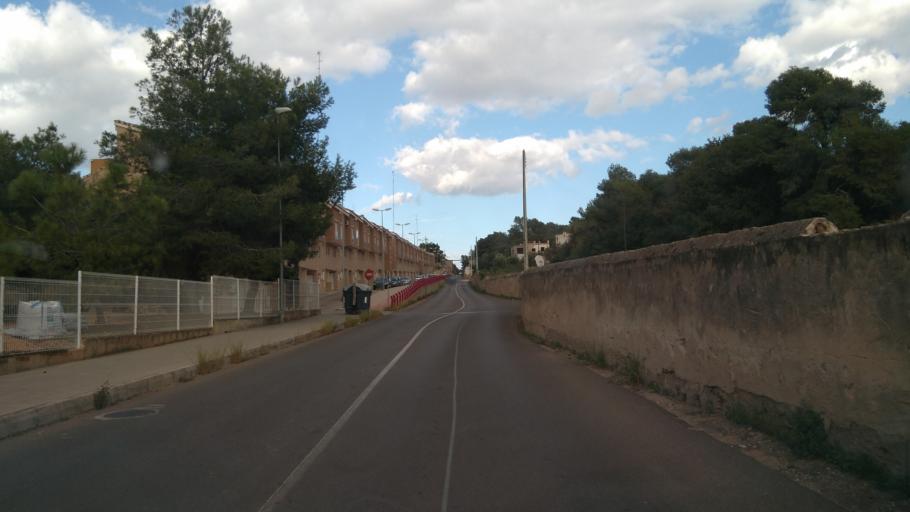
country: ES
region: Valencia
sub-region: Provincia de Valencia
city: Alzira
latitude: 39.1517
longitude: -0.4168
